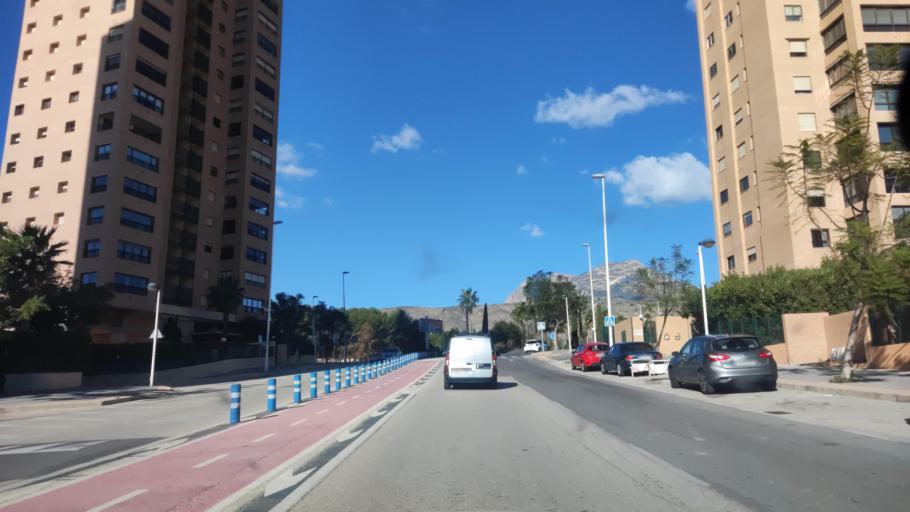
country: ES
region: Valencia
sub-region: Provincia de Alicante
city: Benidorm
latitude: 38.5367
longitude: -0.1576
